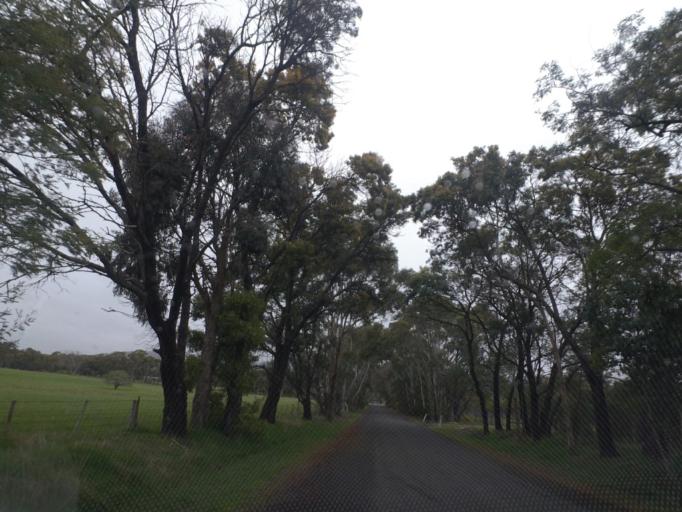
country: AU
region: Victoria
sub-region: Hume
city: Sunbury
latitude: -37.3333
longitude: 144.6050
